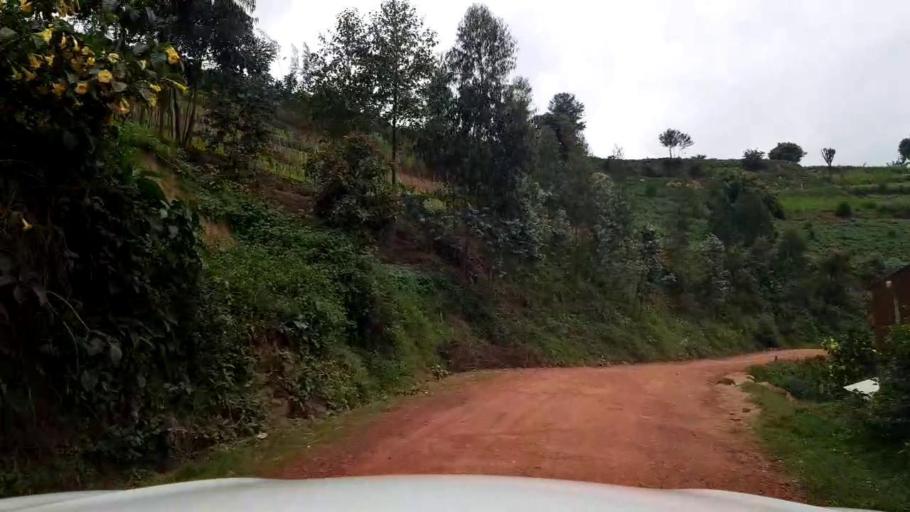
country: RW
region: Northern Province
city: Byumba
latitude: -1.4866
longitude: 29.9292
